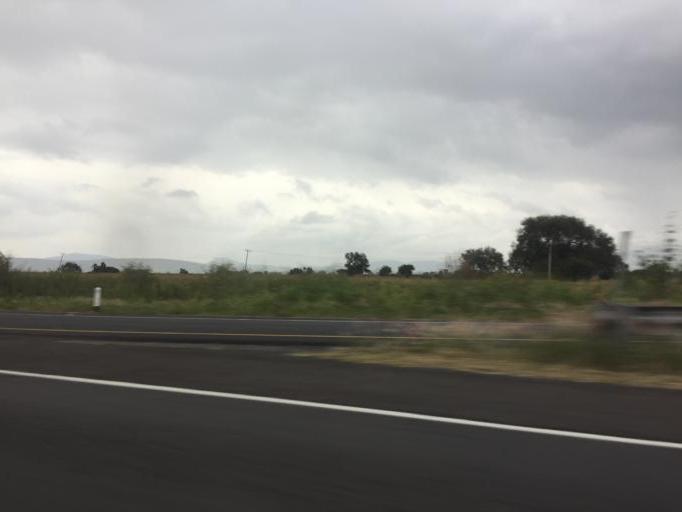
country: MX
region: Jalisco
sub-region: Zapotlan del Rey
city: Zapotlan del Rey
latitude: 20.4667
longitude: -102.9088
